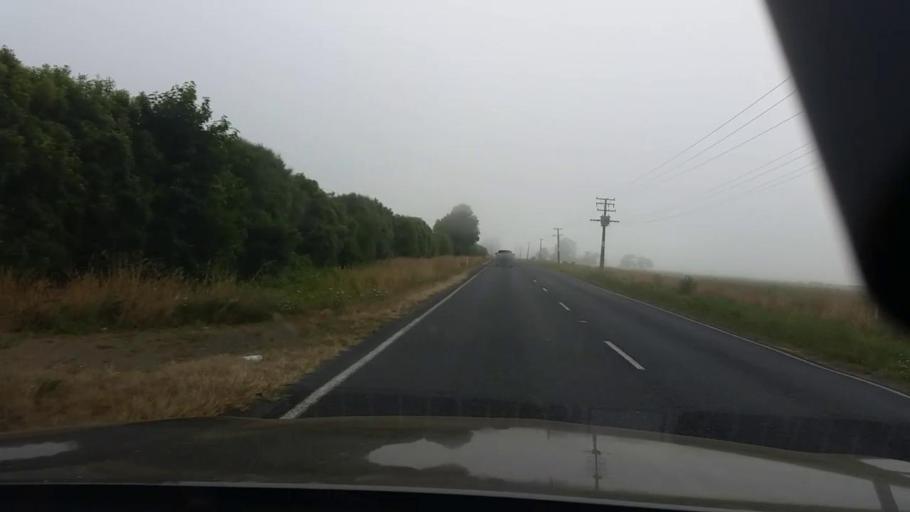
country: NZ
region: Waikato
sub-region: Hamilton City
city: Hamilton
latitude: -37.6353
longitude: 175.3025
